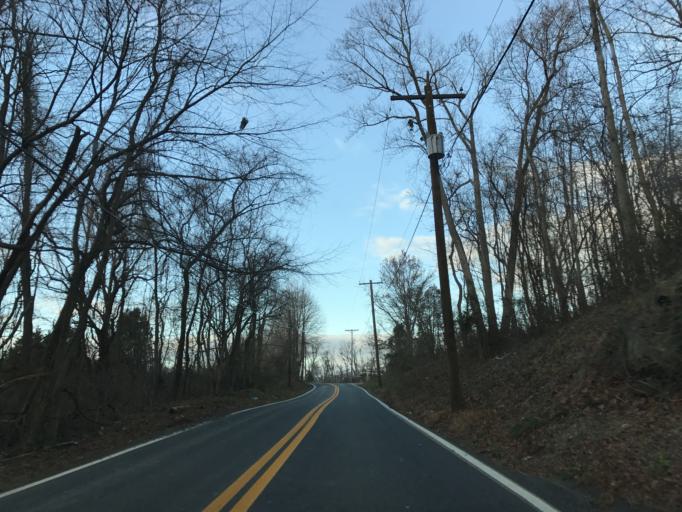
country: US
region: Maryland
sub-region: Cecil County
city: Rising Sun
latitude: 39.6530
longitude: -76.2038
